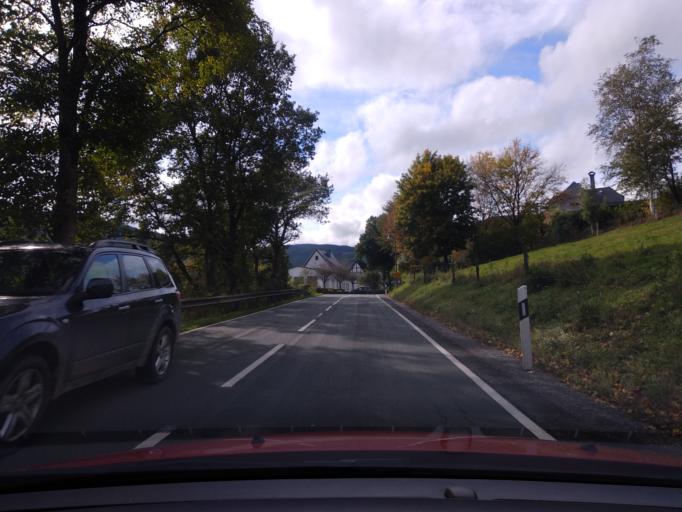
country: DE
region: North Rhine-Westphalia
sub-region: Regierungsbezirk Arnsberg
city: Bad Fredeburg
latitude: 51.2586
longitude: 8.3748
